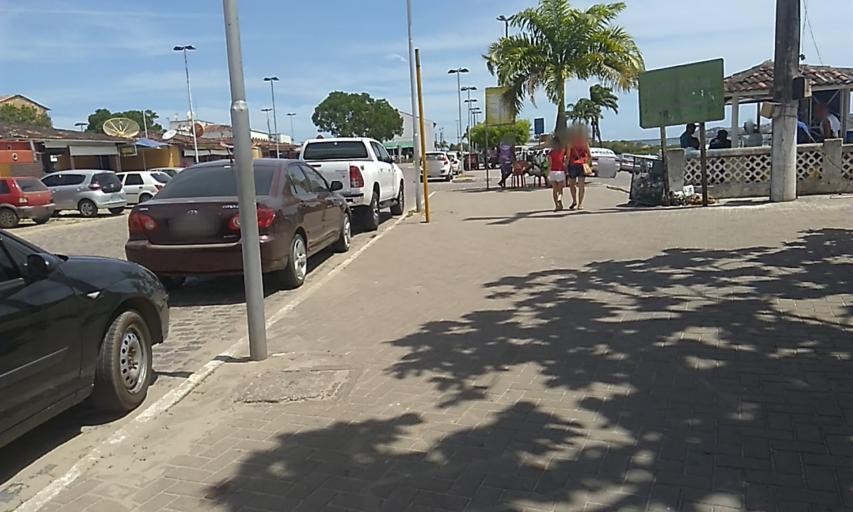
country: BR
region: Alagoas
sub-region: Penedo
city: Penedo
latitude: -10.2920
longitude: -36.5860
